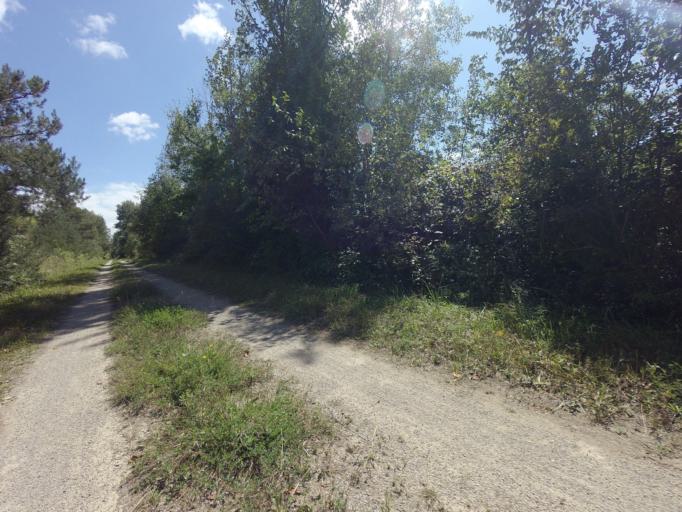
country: CA
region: Ontario
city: Orangeville
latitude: 43.7791
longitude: -80.2115
